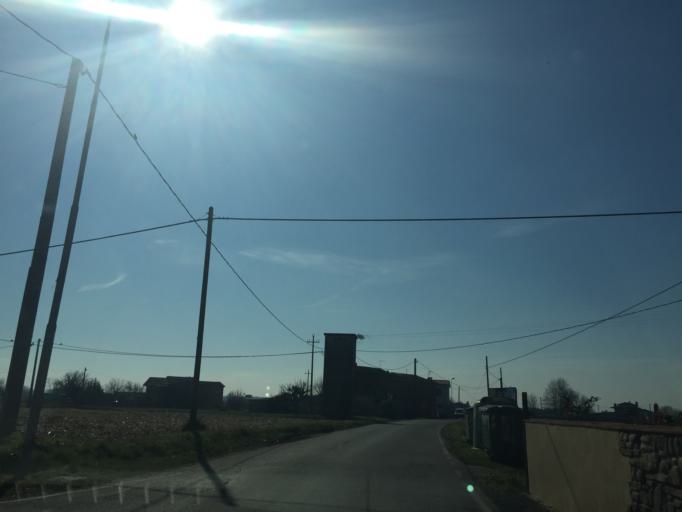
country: IT
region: Tuscany
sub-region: Provincia di Pistoia
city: Ponte Buggianese
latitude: 43.8316
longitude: 10.7428
